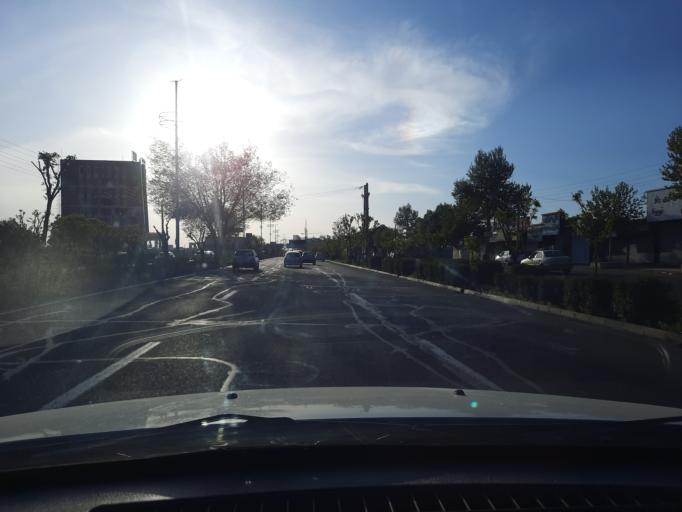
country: IR
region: Qazvin
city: Qazvin
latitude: 36.2640
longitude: 50.0343
